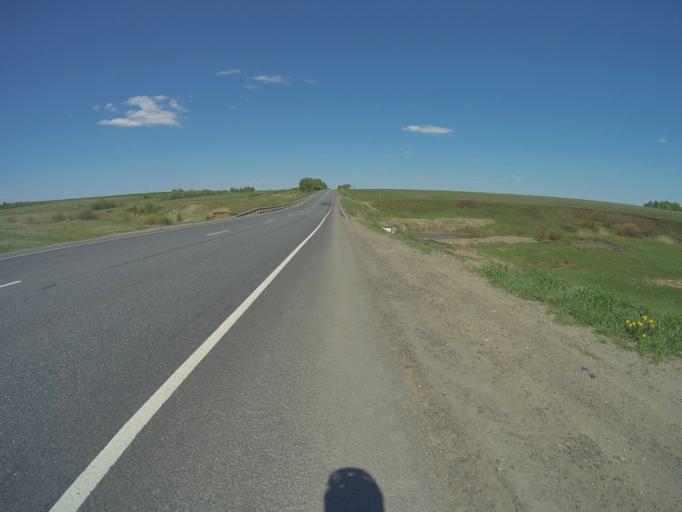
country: RU
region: Vladimir
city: Bogolyubovo
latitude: 56.2871
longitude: 40.4678
